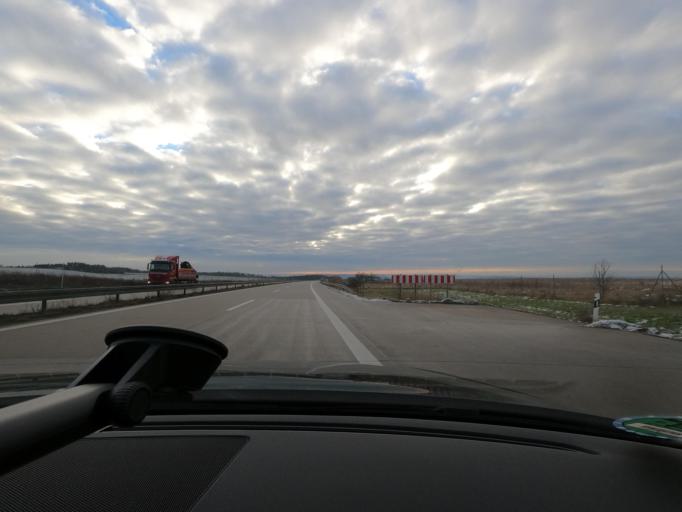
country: DE
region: Bavaria
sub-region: Upper Franconia
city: Meeder
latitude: 50.3388
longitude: 10.9330
